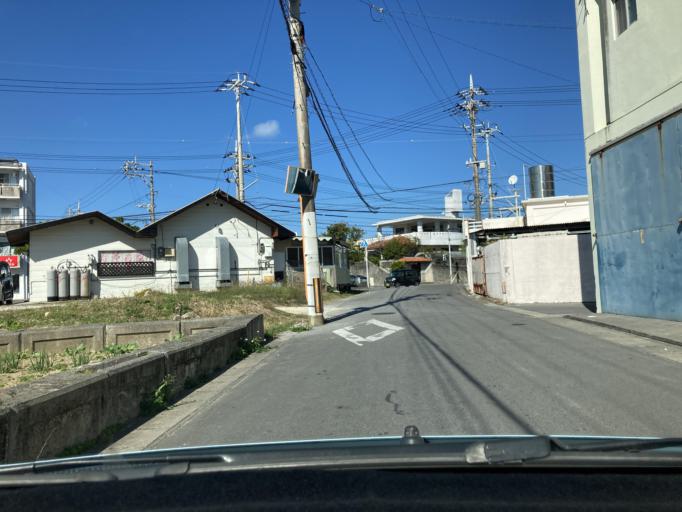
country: JP
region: Okinawa
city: Okinawa
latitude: 26.3459
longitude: 127.8323
